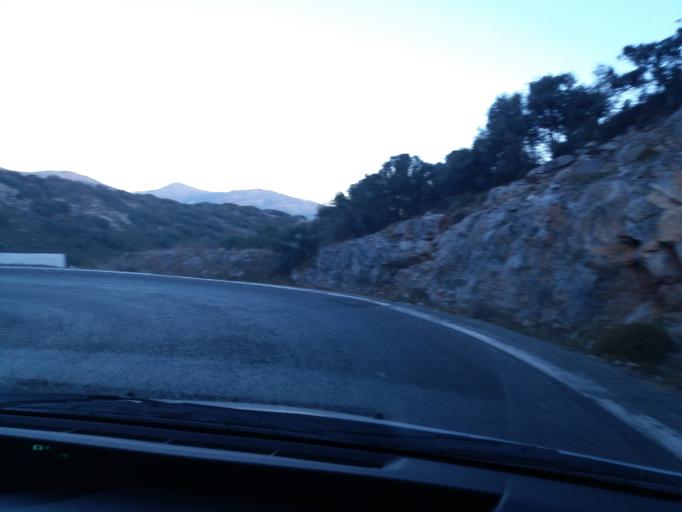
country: GR
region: Crete
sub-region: Nomos Irakleiou
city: Mokhos
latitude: 35.2018
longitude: 25.4568
